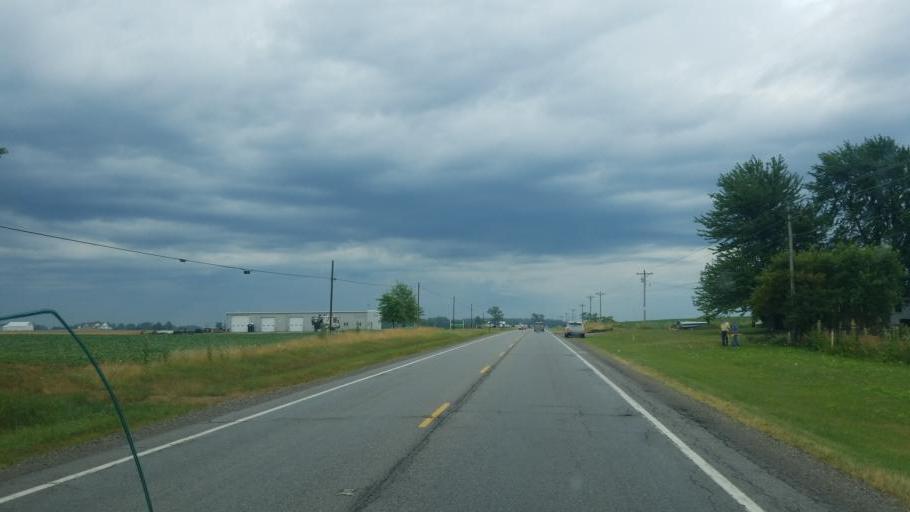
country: US
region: Ohio
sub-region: Williams County
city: Edgerton
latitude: 41.4481
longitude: -84.6985
